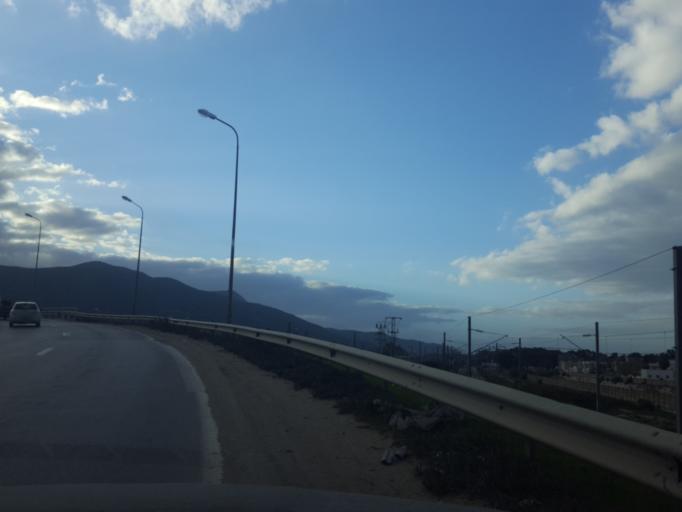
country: TN
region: Tunis
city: Hammam-Lif
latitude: 36.7012
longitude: 10.4043
